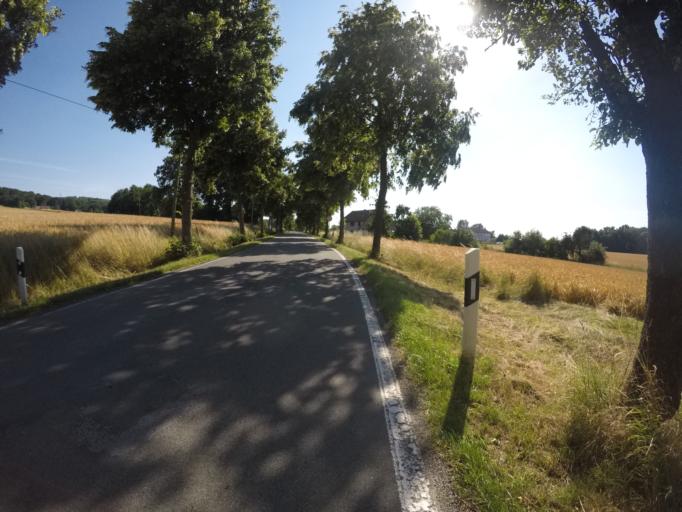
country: DE
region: North Rhine-Westphalia
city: Loehne
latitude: 52.1624
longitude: 8.6974
